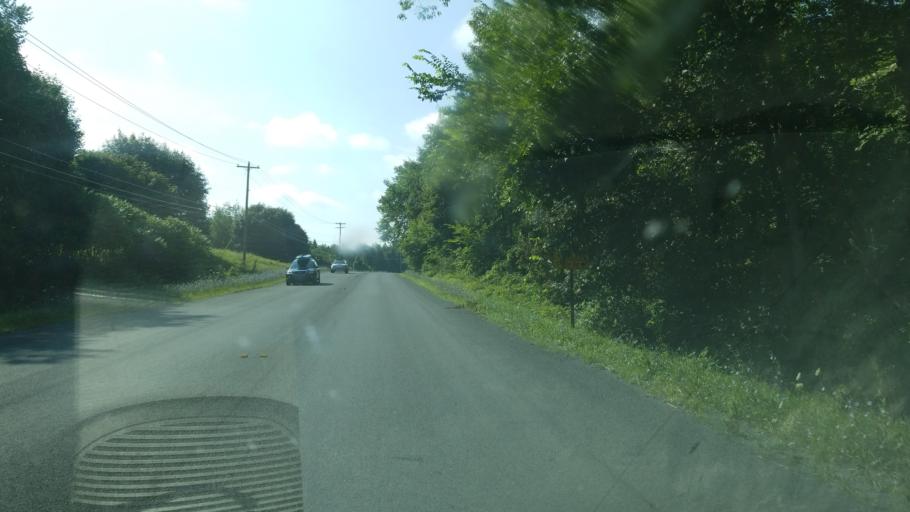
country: US
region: Michigan
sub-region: Kent County
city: Northview
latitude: 43.1033
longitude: -85.6409
